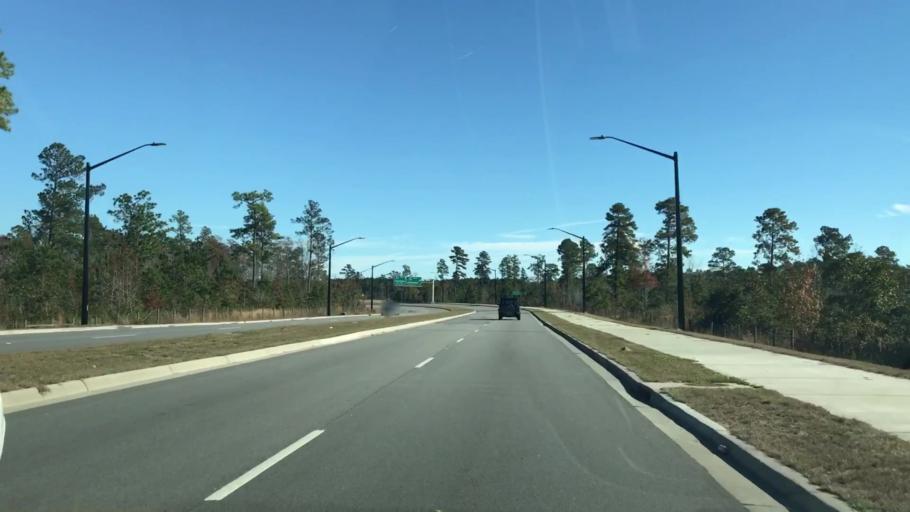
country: US
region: South Carolina
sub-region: Dorchester County
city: Summerville
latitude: 33.0504
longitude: -80.1705
